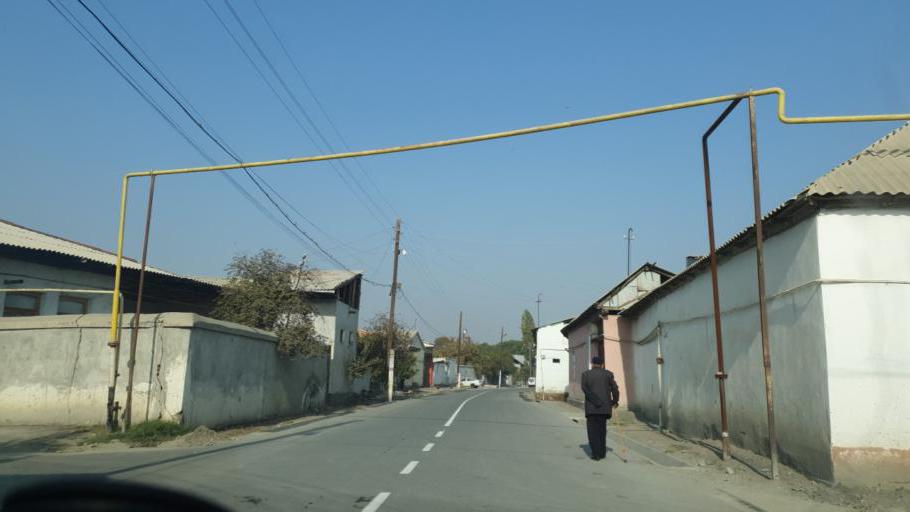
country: UZ
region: Fergana
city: Qo`qon
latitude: 40.5831
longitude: 70.9095
